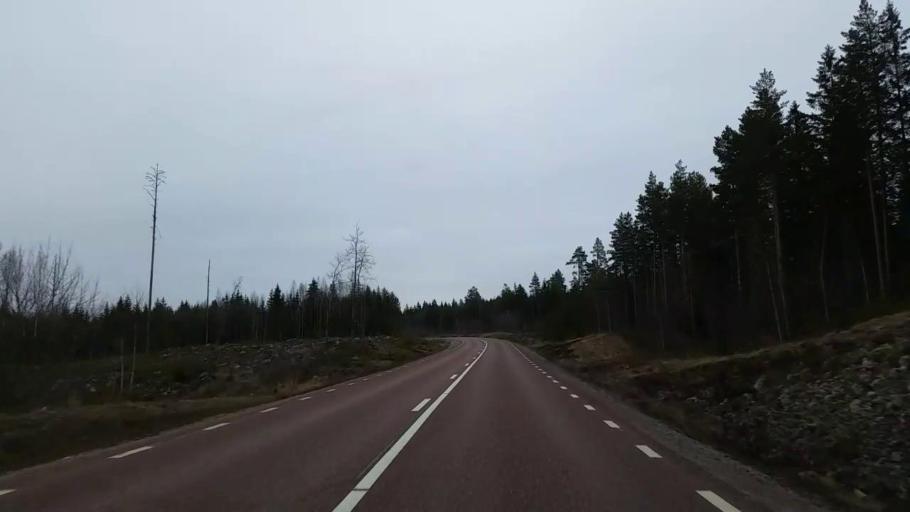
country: SE
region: Gaevleborg
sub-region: Ovanakers Kommun
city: Edsbyn
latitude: 61.2153
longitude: 15.8757
